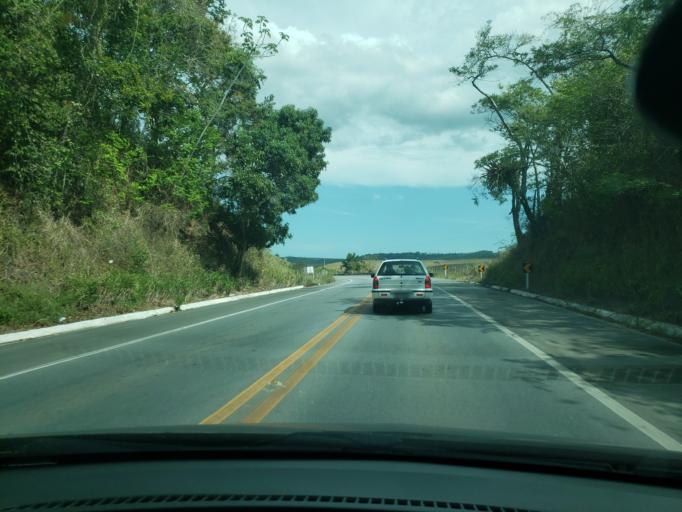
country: BR
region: Alagoas
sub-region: Murici
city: Murici
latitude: -9.3302
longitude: -35.9163
